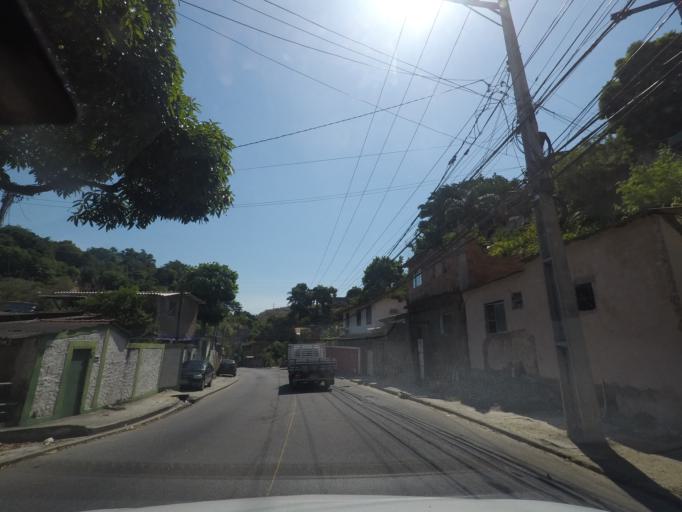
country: BR
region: Rio de Janeiro
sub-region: Niteroi
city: Niteroi
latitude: -22.9054
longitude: -43.0764
